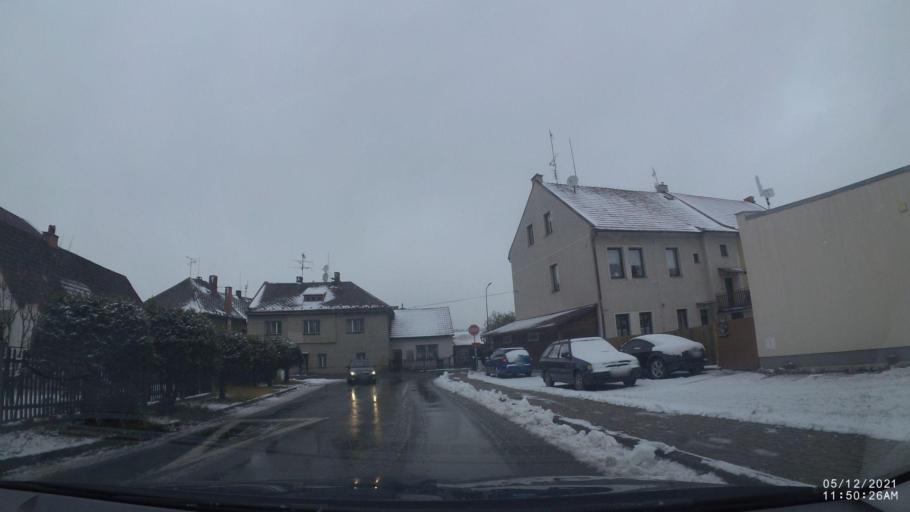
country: CZ
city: Dobruska
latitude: 50.2934
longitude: 16.1644
